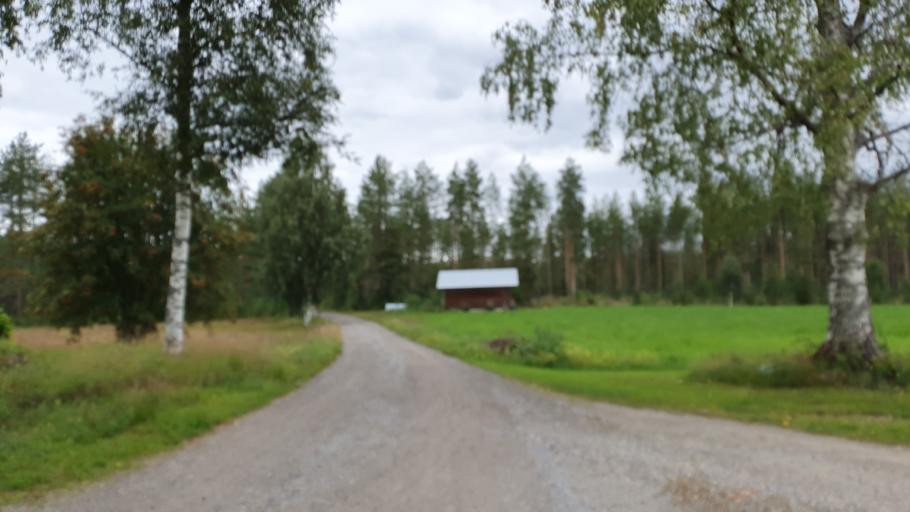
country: FI
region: Kainuu
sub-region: Kehys-Kainuu
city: Kuhmo
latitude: 64.1257
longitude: 29.4592
